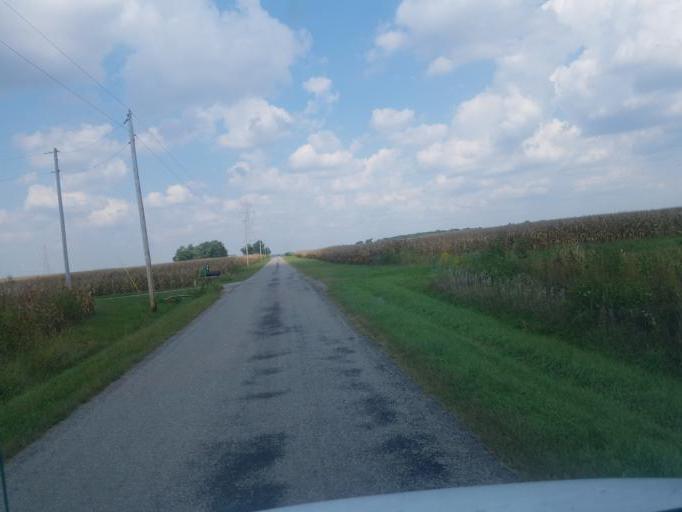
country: US
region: Ohio
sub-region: Hardin County
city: Ada
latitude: 40.6245
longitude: -83.7876
